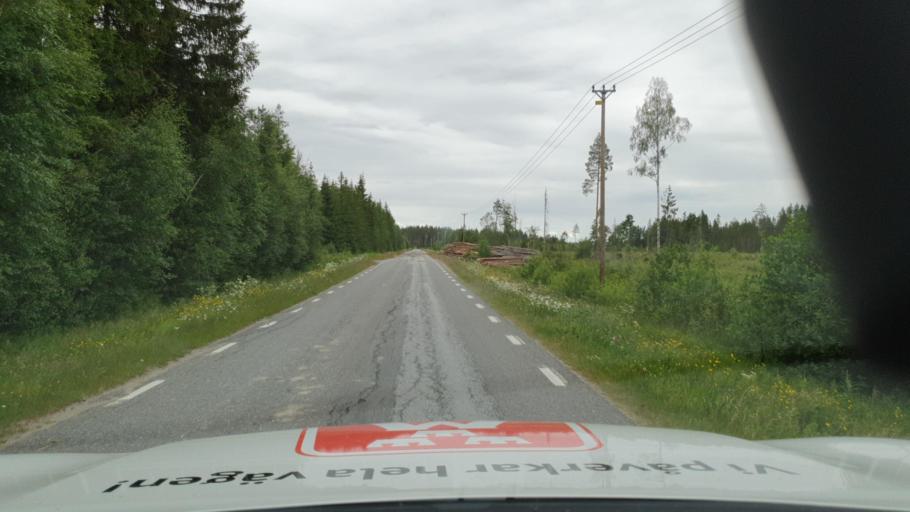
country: SE
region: Vaesterbotten
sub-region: Nordmalings Kommun
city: Nordmaling
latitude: 63.5123
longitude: 19.4212
